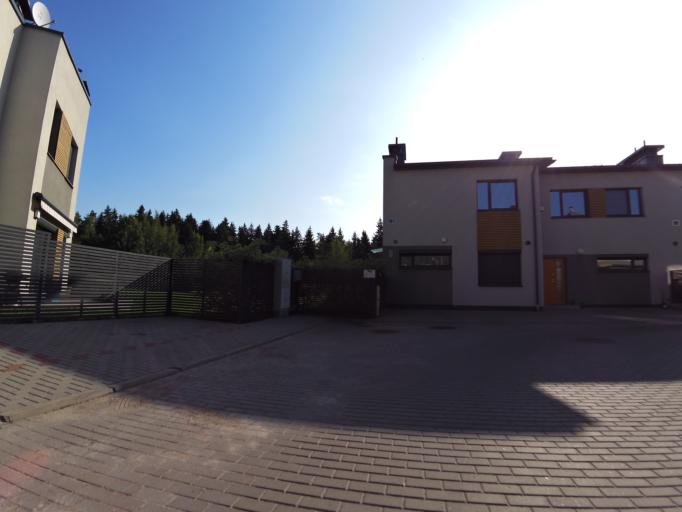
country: LT
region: Vilnius County
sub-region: Vilnius
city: Fabijoniskes
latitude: 54.7644
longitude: 25.2870
